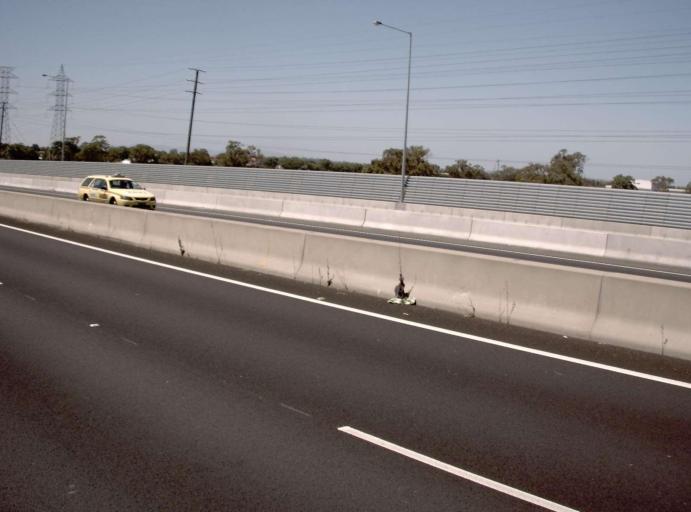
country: AU
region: Victoria
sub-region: Hume
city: Campbellfield
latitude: -37.6921
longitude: 144.9504
